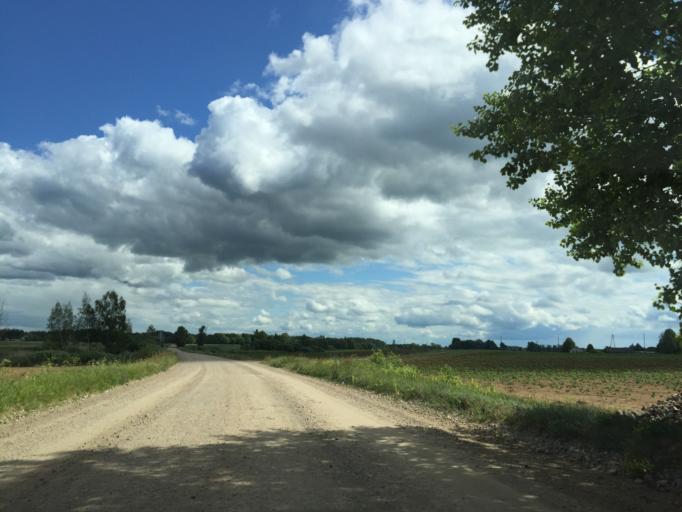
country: LV
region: Lecava
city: Iecava
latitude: 56.5069
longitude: 24.3511
